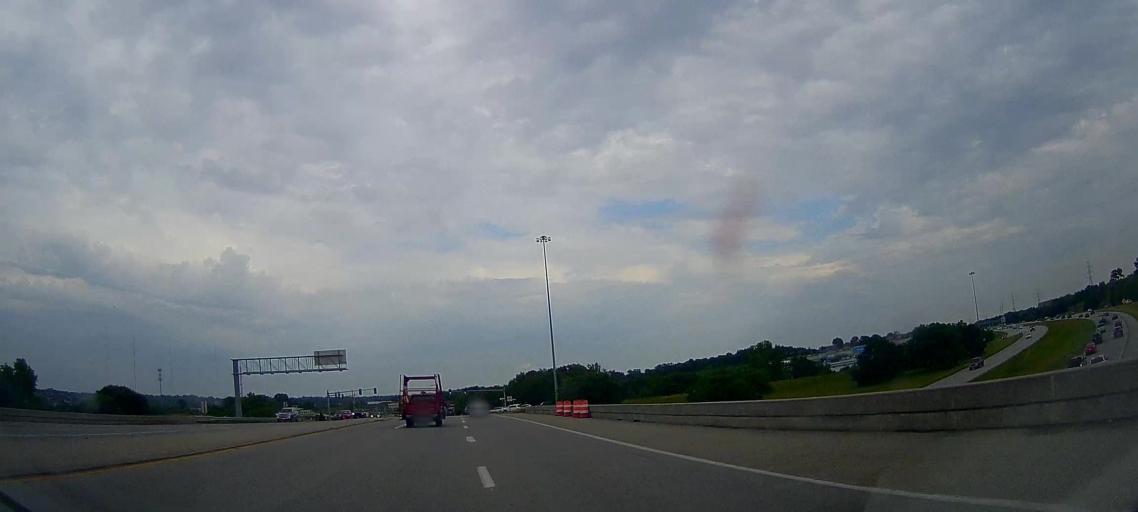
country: US
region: Nebraska
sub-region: Douglas County
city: Bennington
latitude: 41.3220
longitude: -96.0691
